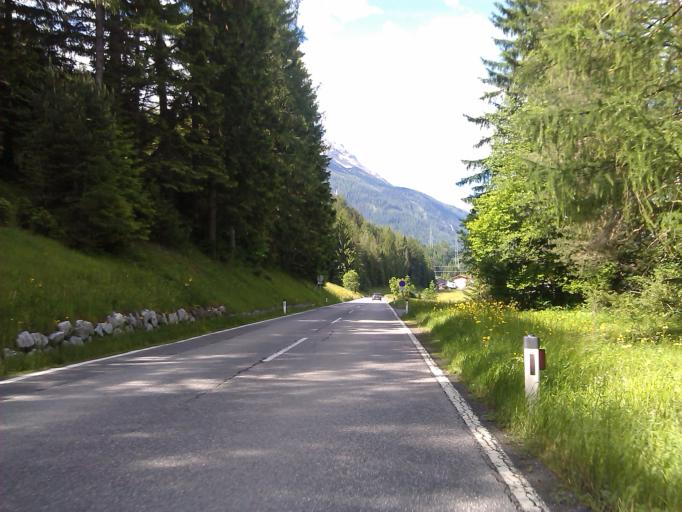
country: AT
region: Tyrol
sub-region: Politischer Bezirk Reutte
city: Biberwier
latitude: 47.3864
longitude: 10.9093
